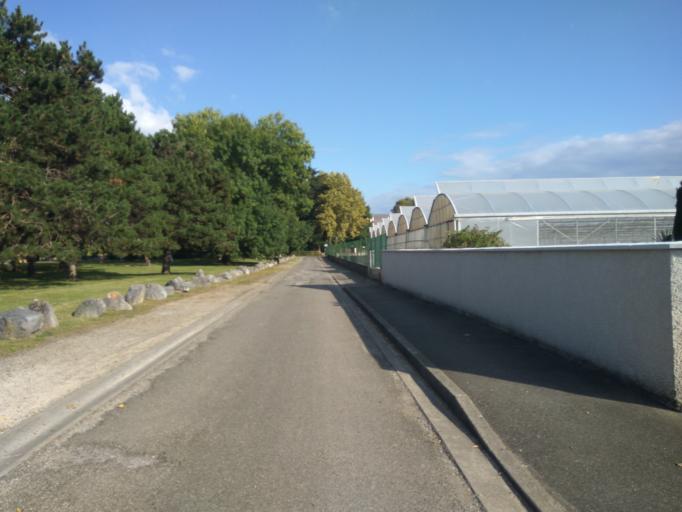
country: FR
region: Aquitaine
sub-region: Departement des Pyrenees-Atlantiques
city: Gelos
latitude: 43.2872
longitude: -0.3715
